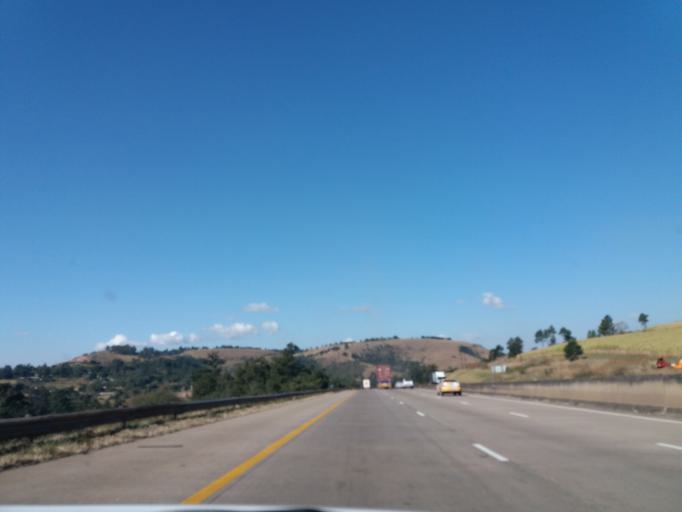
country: ZA
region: KwaZulu-Natal
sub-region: eThekwini Metropolitan Municipality
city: Mpumalanga
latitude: -29.7369
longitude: 30.6493
